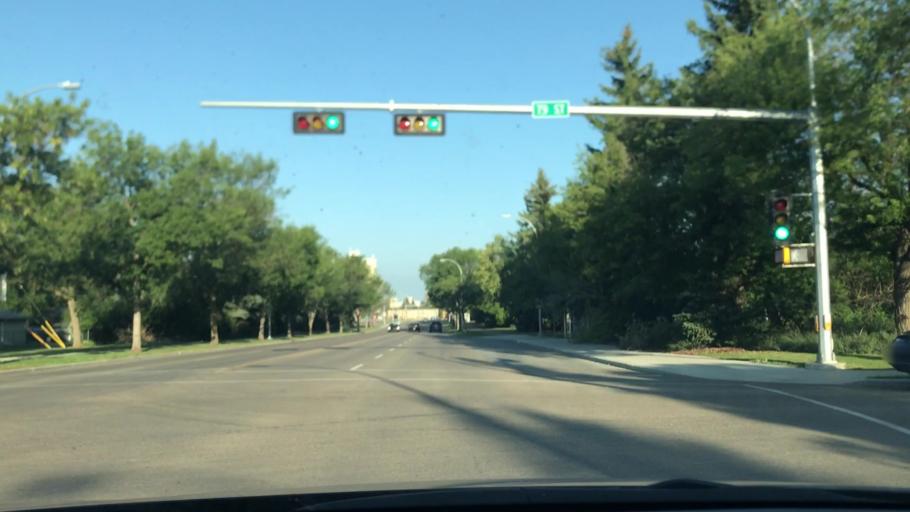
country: CA
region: Alberta
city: Edmonton
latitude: 53.5253
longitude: -113.4491
